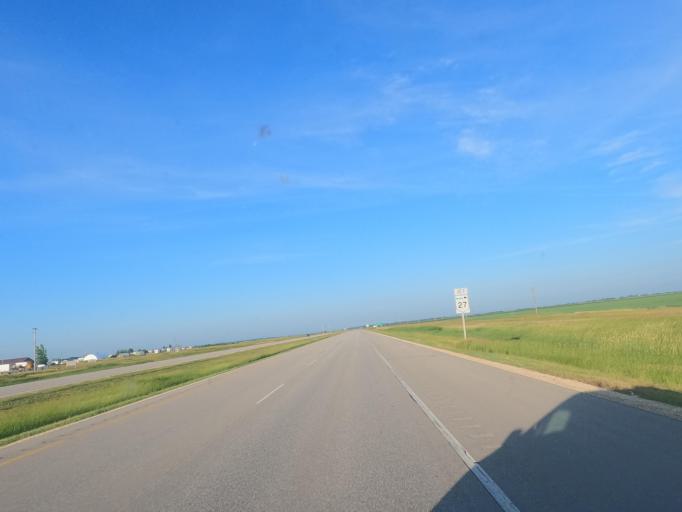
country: CA
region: Manitoba
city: Selkirk
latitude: 50.0570
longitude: -97.0540
